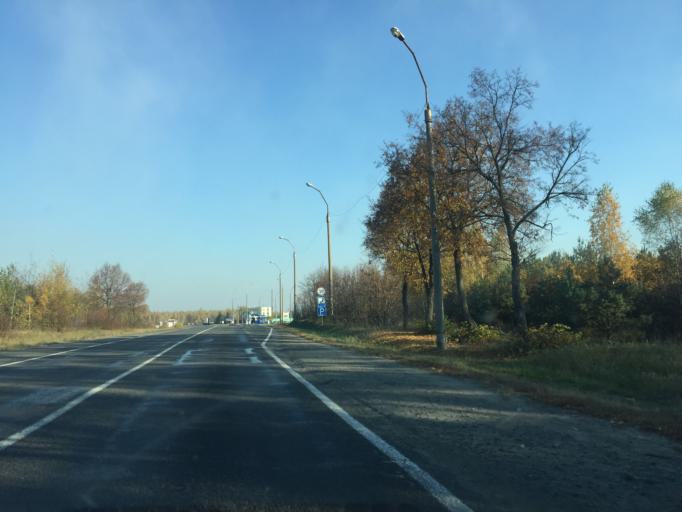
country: BY
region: Gomel
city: Dobrush
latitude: 52.3884
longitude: 31.4610
